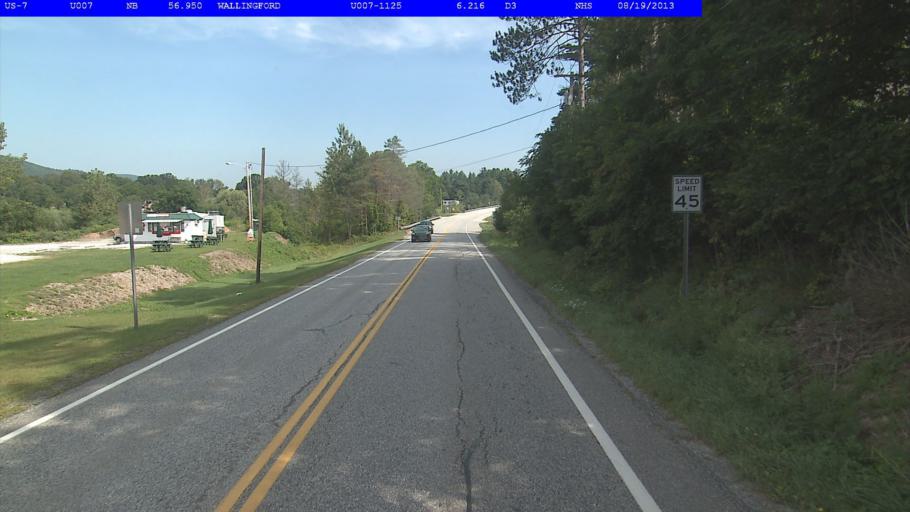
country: US
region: Vermont
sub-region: Rutland County
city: Rutland
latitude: 43.4820
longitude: -72.9740
